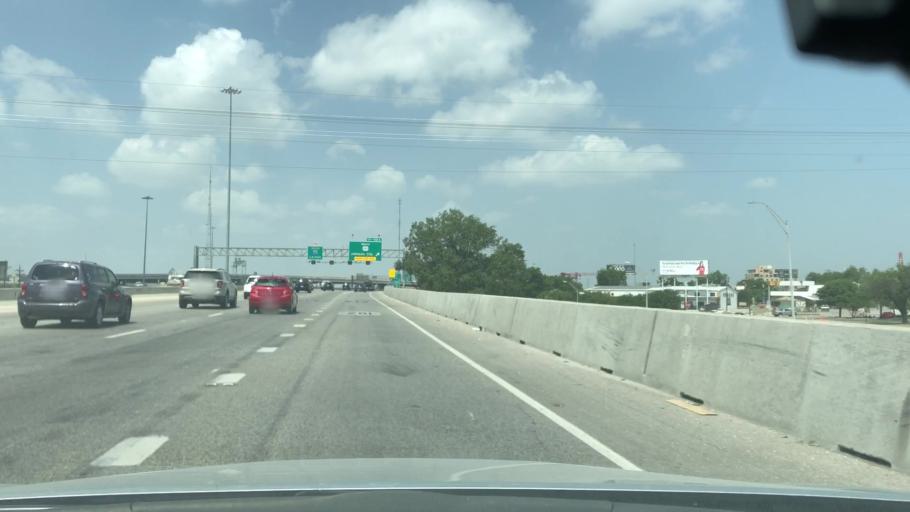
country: US
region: Texas
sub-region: Bexar County
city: San Antonio
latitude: 29.4398
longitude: -98.4725
